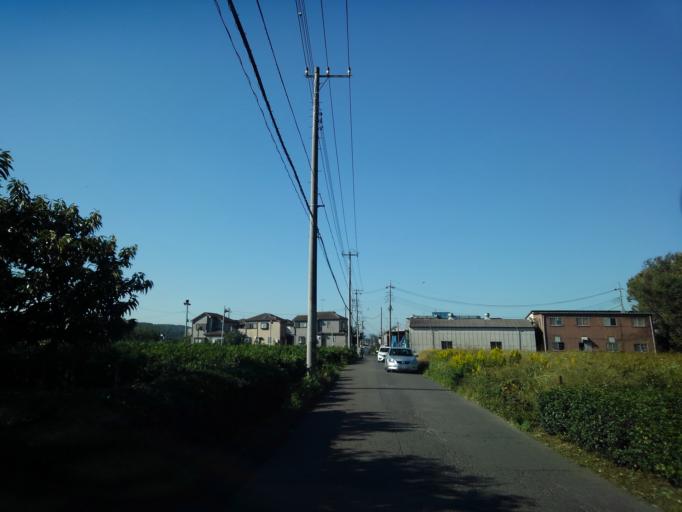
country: JP
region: Saitama
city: Sayama
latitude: 35.7963
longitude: 139.3900
